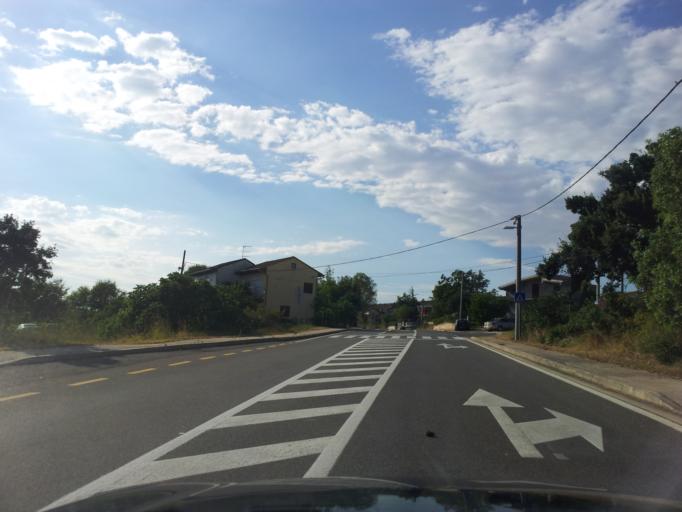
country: HR
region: Zadarska
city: Posedarje
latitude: 44.2154
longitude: 15.4680
